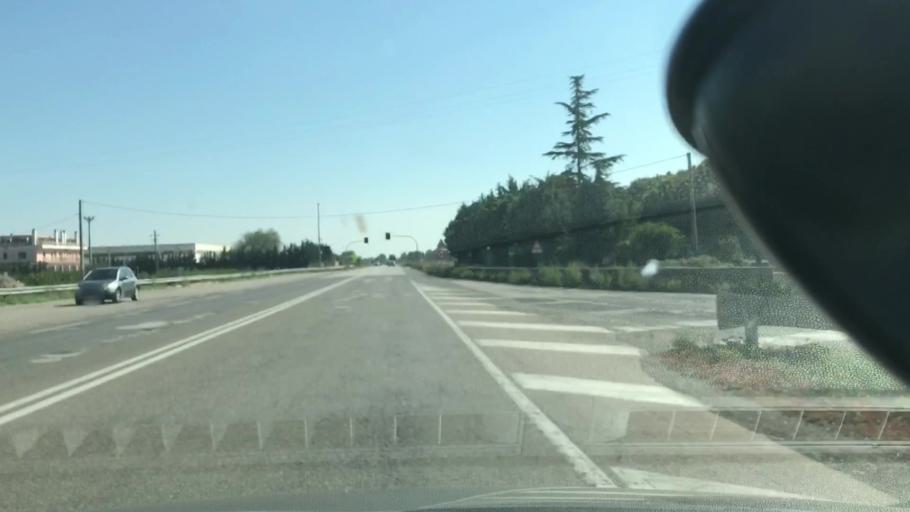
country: IT
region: Apulia
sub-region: Provincia di Foggia
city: Foggia
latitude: 41.4266
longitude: 15.5650
